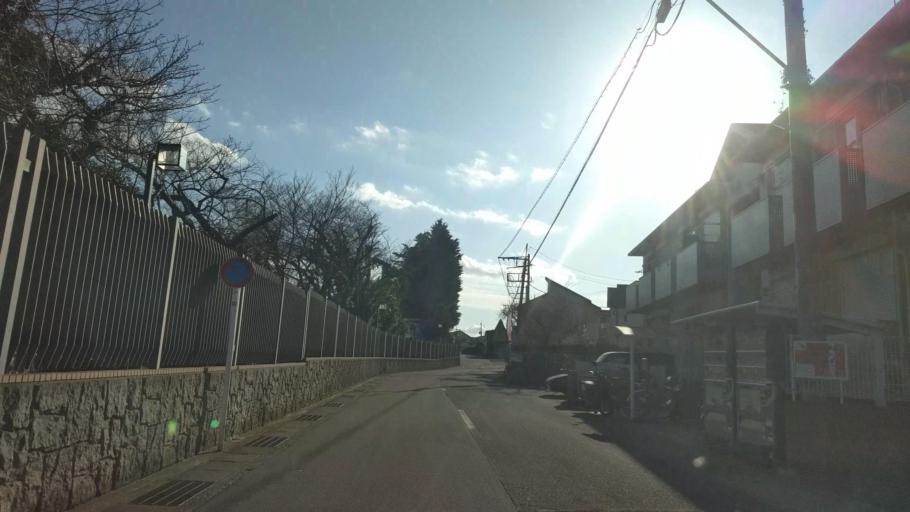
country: JP
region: Kanagawa
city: Isehara
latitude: 35.3631
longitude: 139.2714
